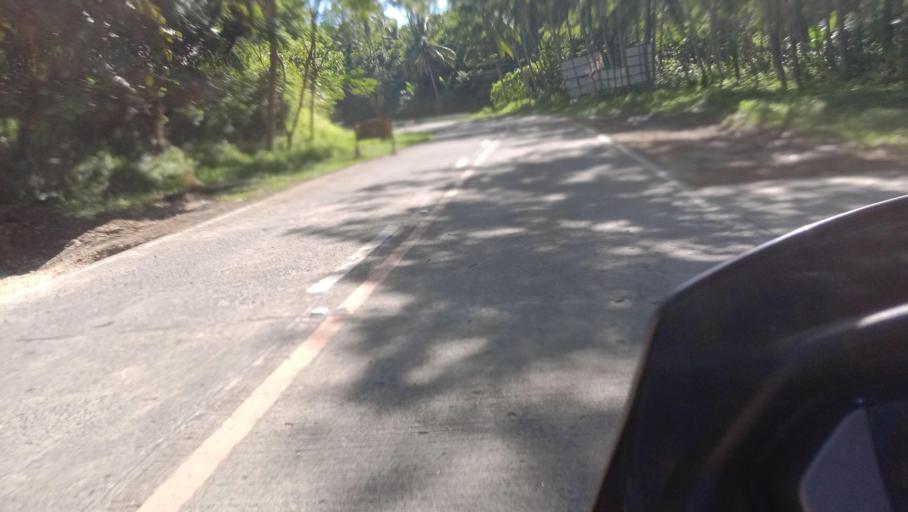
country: PH
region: Caraga
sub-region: Province of Surigao del Sur
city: Barobo
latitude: 8.5370
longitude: 126.1032
